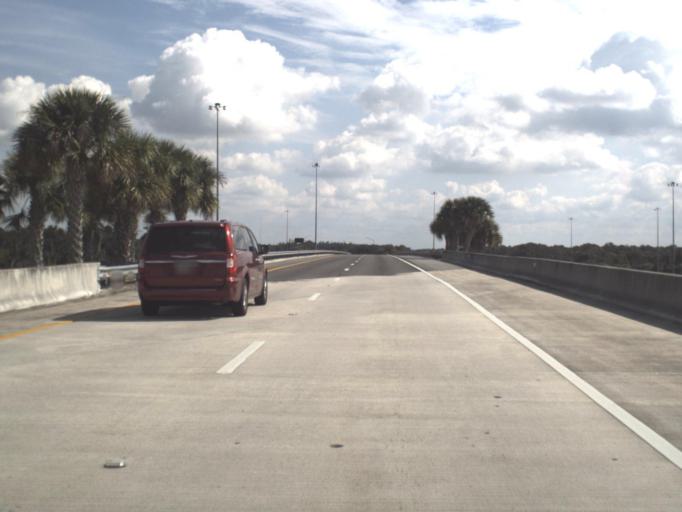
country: US
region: Florida
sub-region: Polk County
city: Fussels Corner
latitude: 28.0104
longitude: -81.8472
